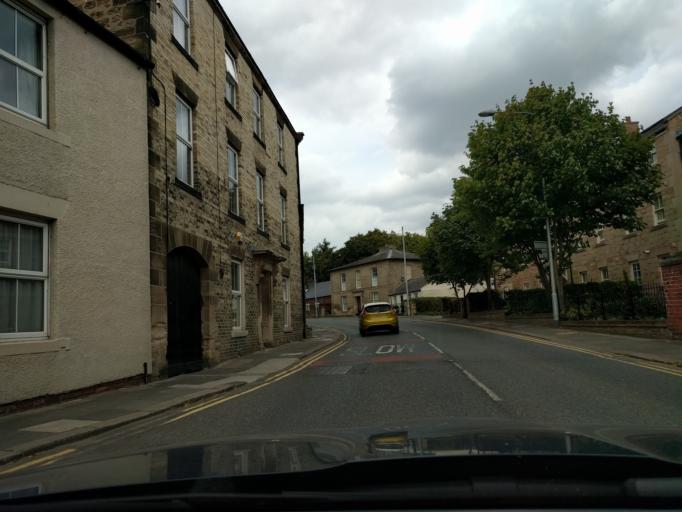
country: GB
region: England
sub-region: Northumberland
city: Morpeth
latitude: 55.1718
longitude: -1.6950
